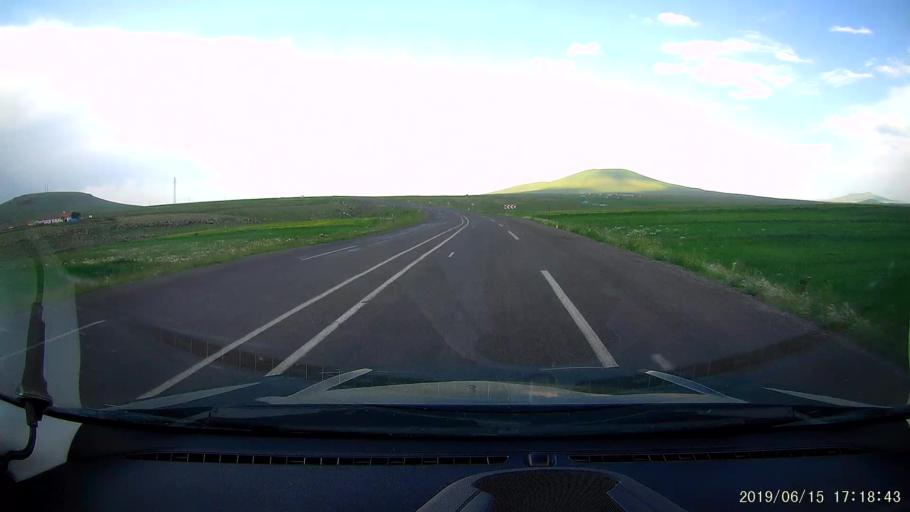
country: TR
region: Kars
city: Kars
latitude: 40.6131
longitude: 43.2640
